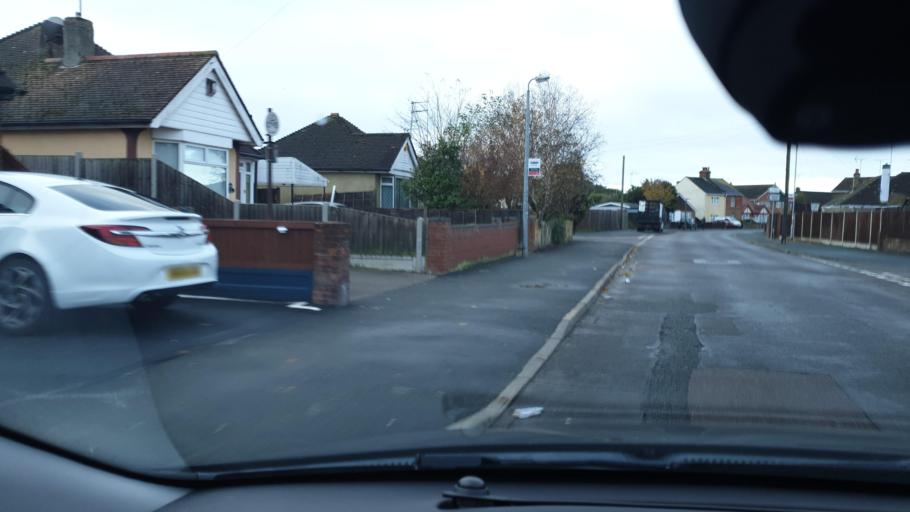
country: GB
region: England
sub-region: Essex
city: Clacton-on-Sea
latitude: 51.7939
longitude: 1.1395
